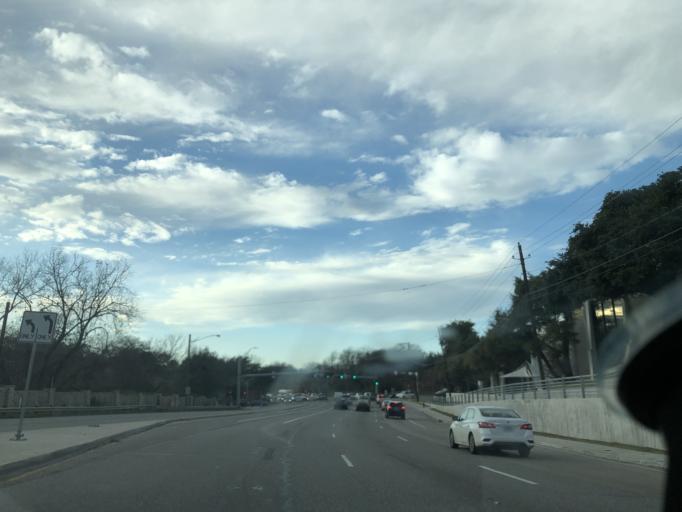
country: US
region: Texas
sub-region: Dallas County
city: University Park
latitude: 32.8659
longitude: -96.8208
